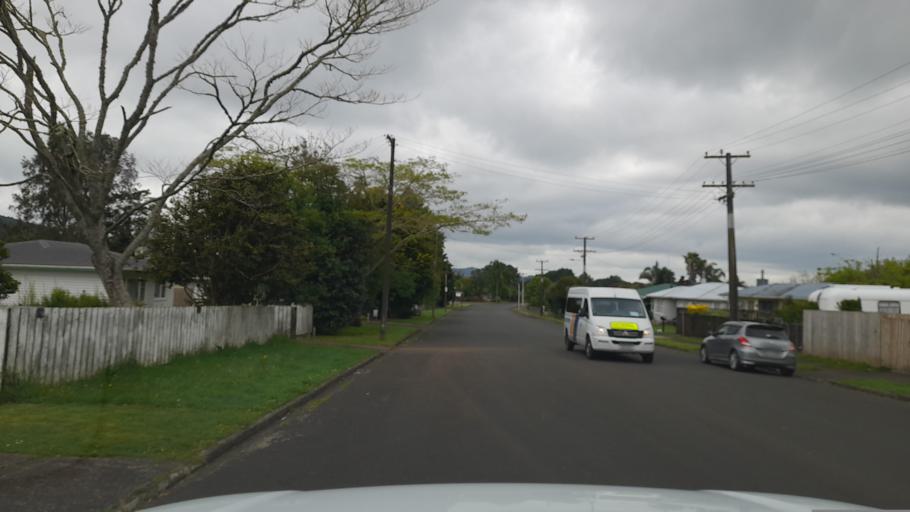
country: NZ
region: Northland
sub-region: Far North District
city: Waimate North
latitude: -35.4040
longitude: 173.7887
